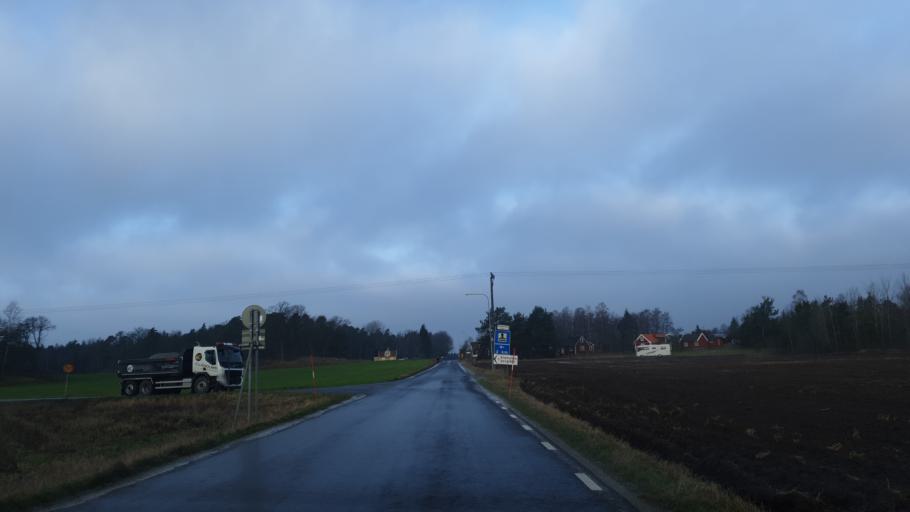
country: SE
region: Blekinge
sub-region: Karlshamns Kommun
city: Morrum
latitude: 56.1694
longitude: 14.7436
